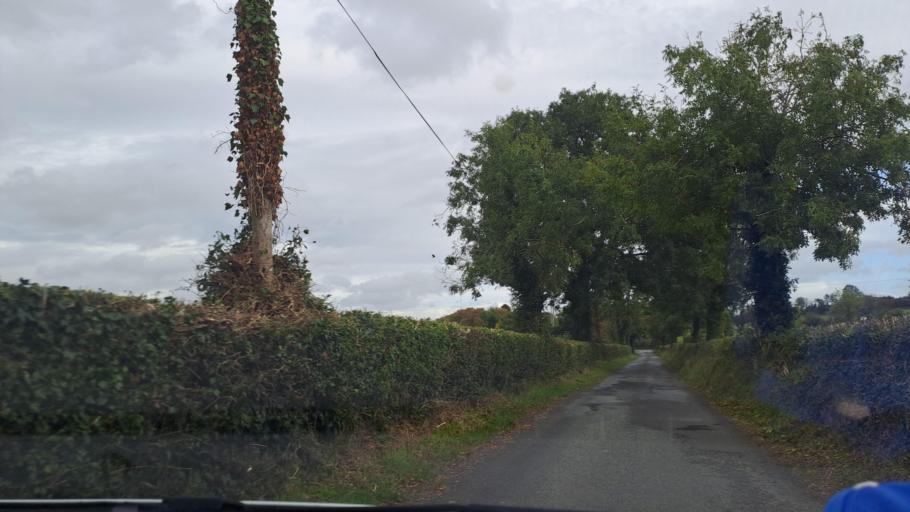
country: IE
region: Ulster
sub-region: An Cabhan
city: Kingscourt
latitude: 53.9398
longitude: -6.8091
